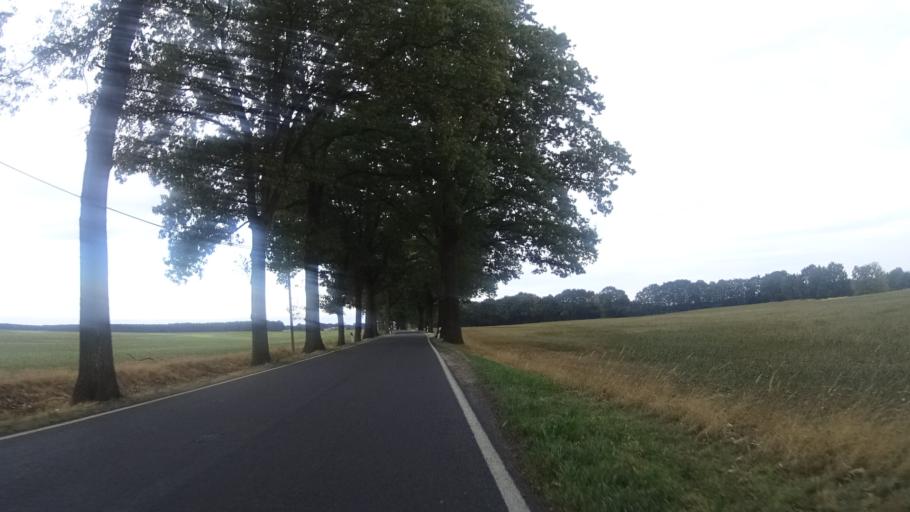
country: DE
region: Saxony
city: Rothenburg
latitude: 51.3015
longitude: 15.0097
